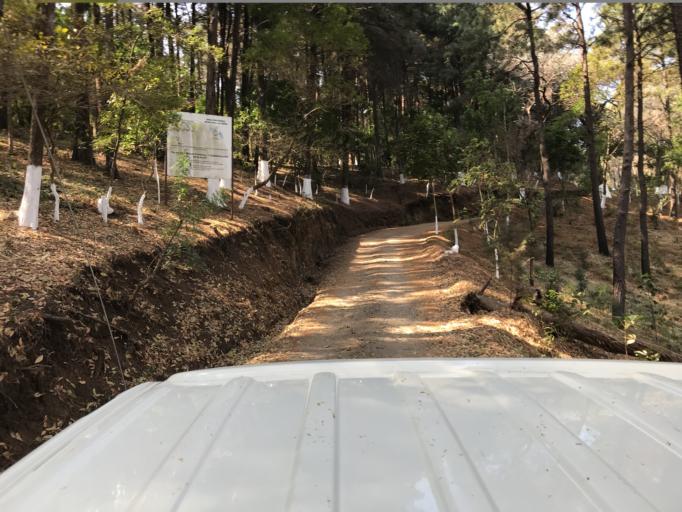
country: GT
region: Guatemala
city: Petapa
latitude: 14.4851
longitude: -90.5554
